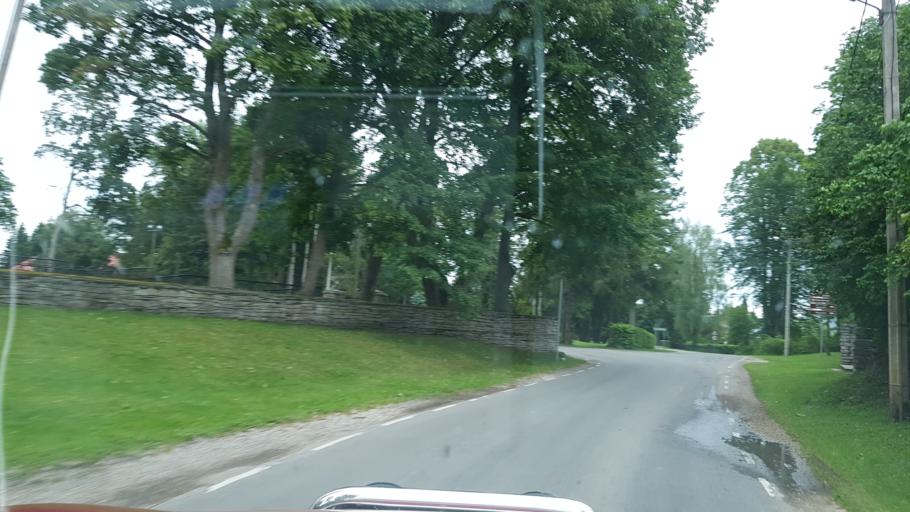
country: EE
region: Harju
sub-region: Nissi vald
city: Turba
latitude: 58.8809
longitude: 24.0752
